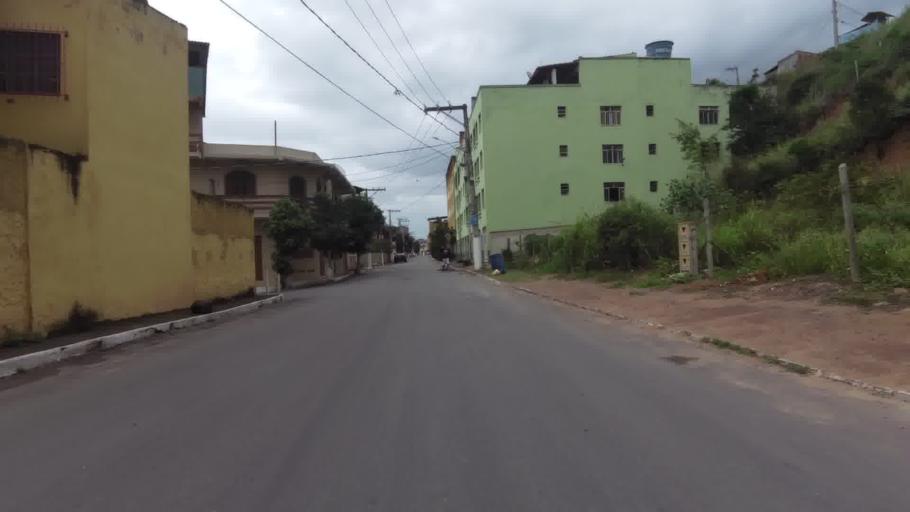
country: BR
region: Espirito Santo
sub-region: Marataizes
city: Marataizes
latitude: -21.0462
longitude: -40.8321
